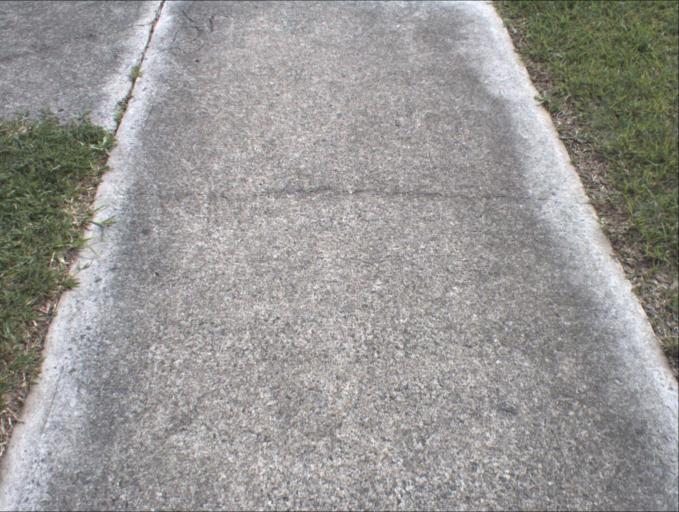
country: AU
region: Queensland
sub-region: Logan
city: Cedar Vale
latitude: -27.8299
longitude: 153.0293
